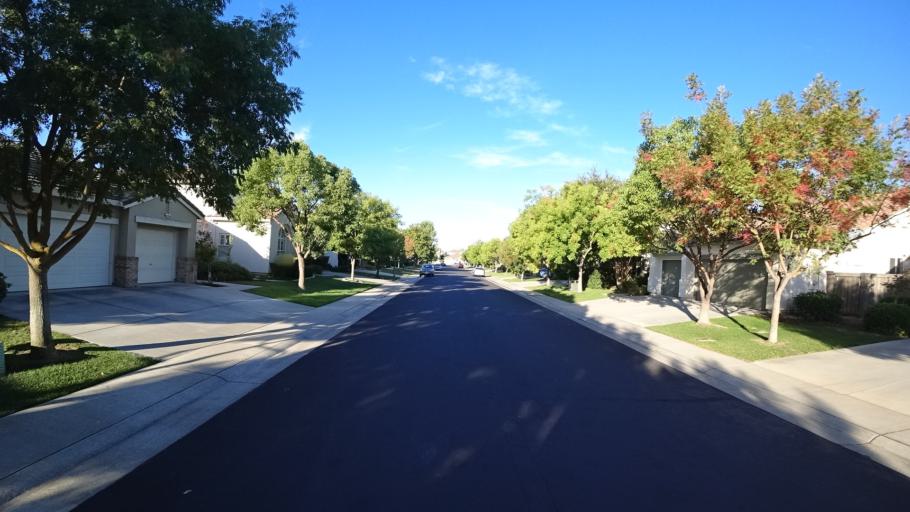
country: US
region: California
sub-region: Sacramento County
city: Laguna
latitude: 38.4004
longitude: -121.4769
